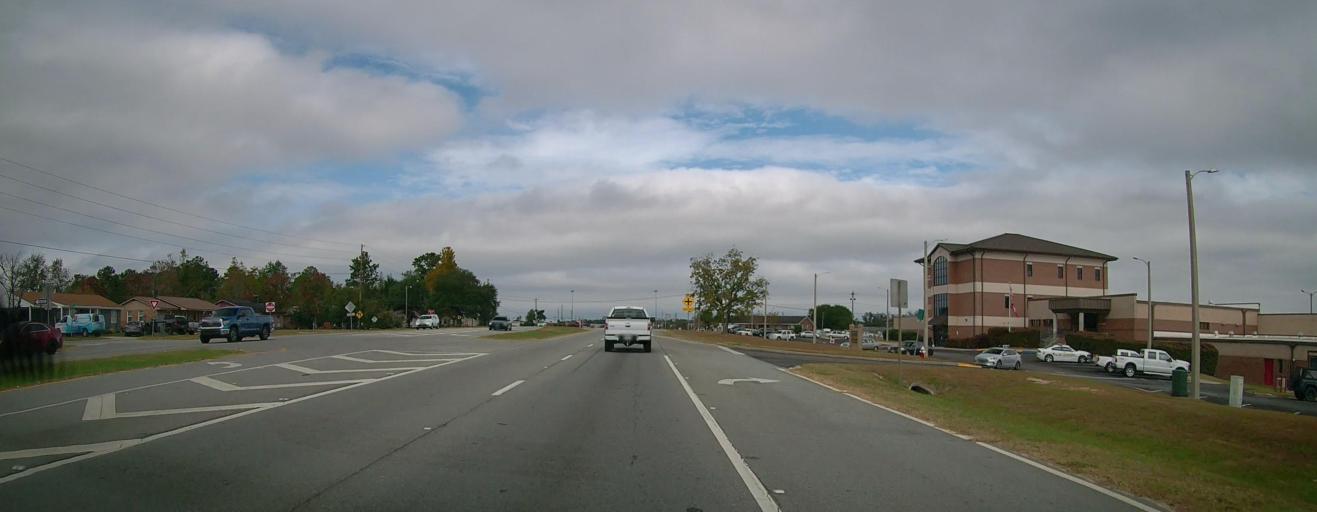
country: US
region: Georgia
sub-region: Colquitt County
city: Moultrie
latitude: 31.1816
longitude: -83.7618
